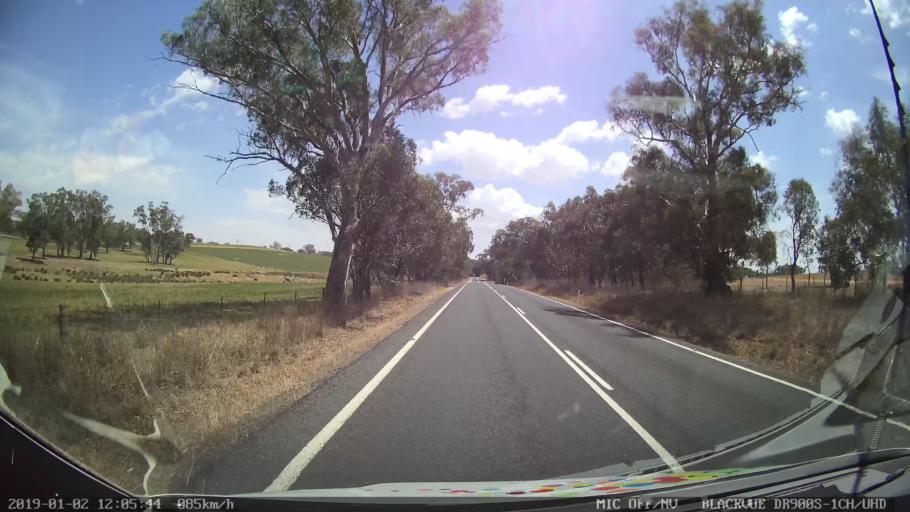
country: AU
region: New South Wales
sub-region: Young
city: Young
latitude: -34.5109
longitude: 148.2997
